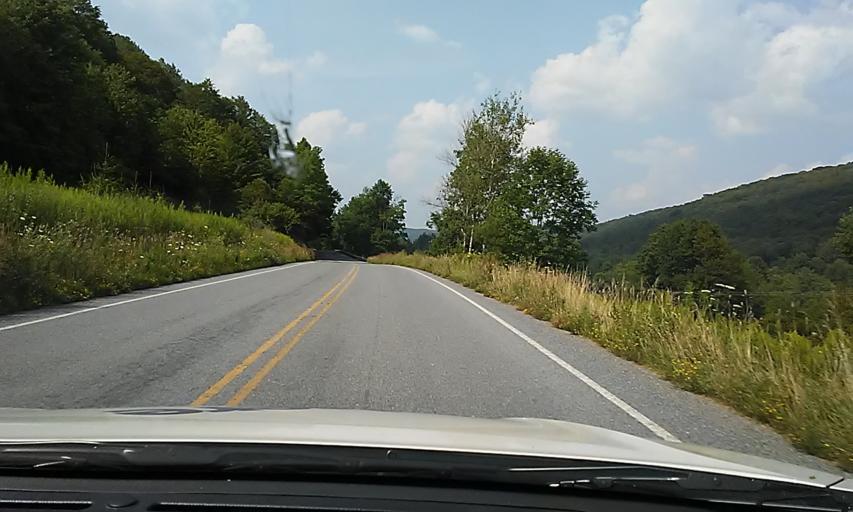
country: US
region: Pennsylvania
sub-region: Potter County
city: Coudersport
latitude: 41.8880
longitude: -77.8430
